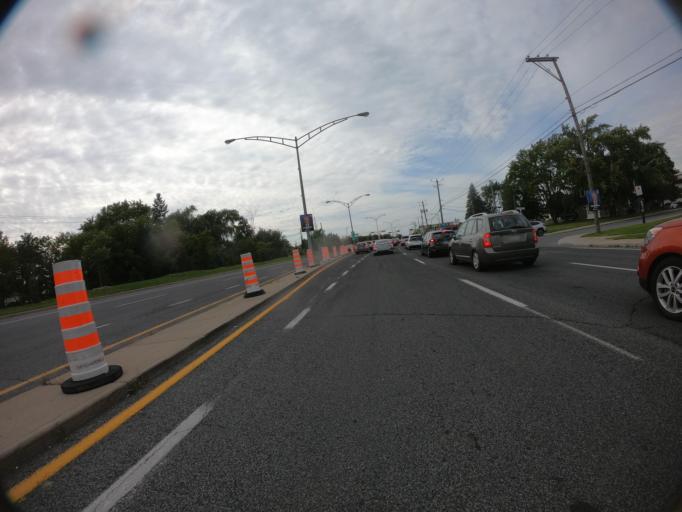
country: CA
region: Quebec
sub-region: Monteregie
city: Chambly
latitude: 45.4454
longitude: -73.2854
